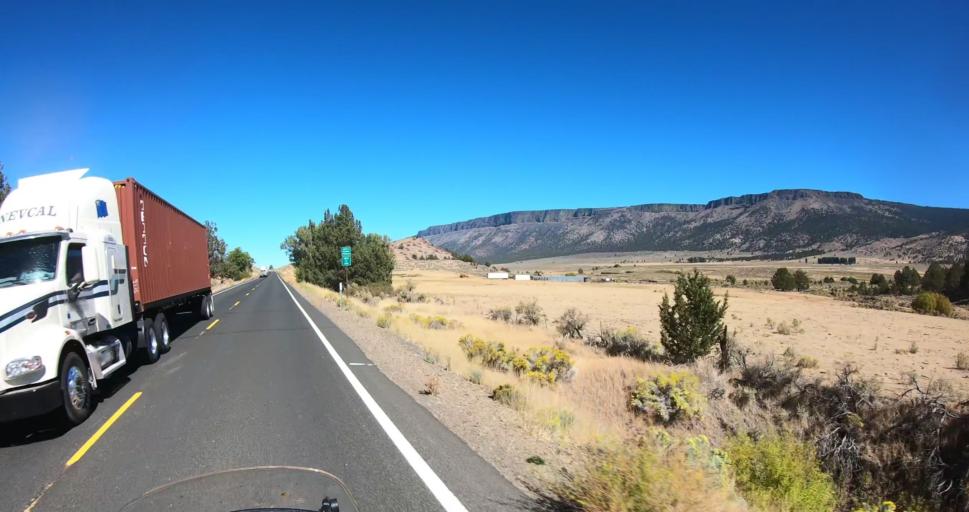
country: US
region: Oregon
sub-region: Lake County
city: Lakeview
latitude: 42.4339
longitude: -120.2816
